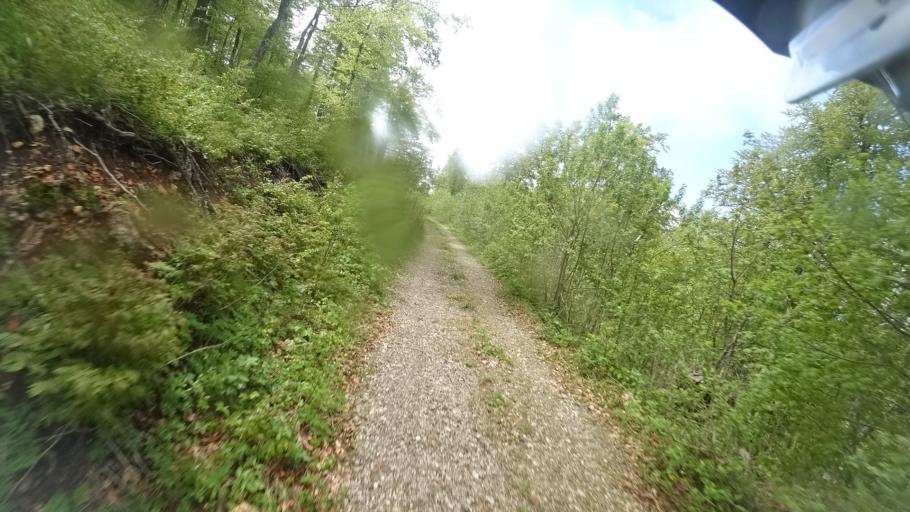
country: BA
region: Federation of Bosnia and Herzegovina
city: Orasac
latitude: 44.5763
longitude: 15.8728
